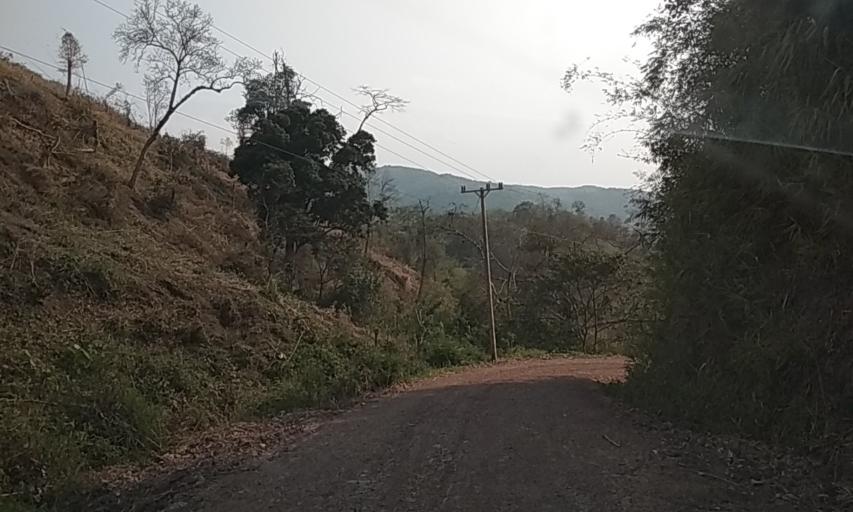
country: LA
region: Louangphabang
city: Louangphabang
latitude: 20.0399
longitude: 101.7999
